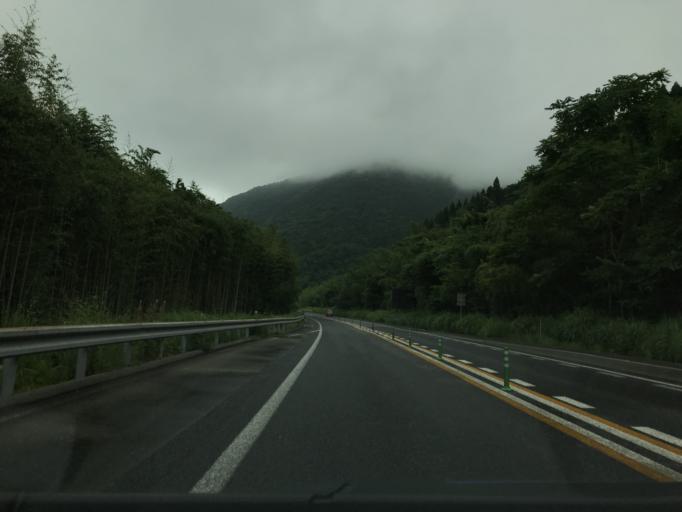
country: JP
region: Oita
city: Bungo-Takada-shi
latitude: 33.4922
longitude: 131.3208
